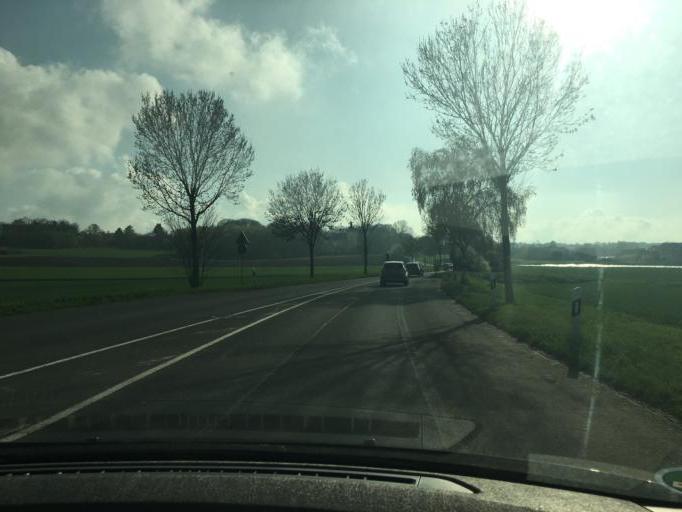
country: DE
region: North Rhine-Westphalia
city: Bornheim
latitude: 50.7614
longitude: 6.9741
